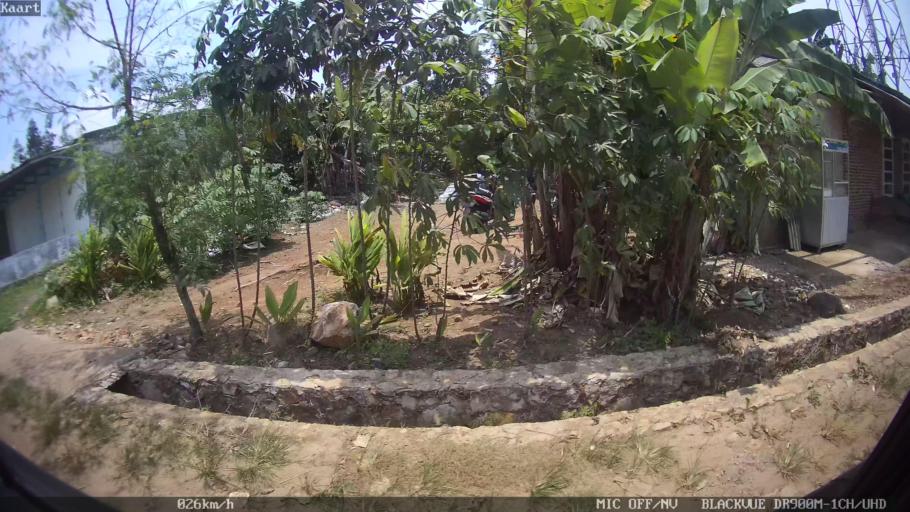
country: ID
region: Lampung
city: Kedaton
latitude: -5.3260
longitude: 105.2501
